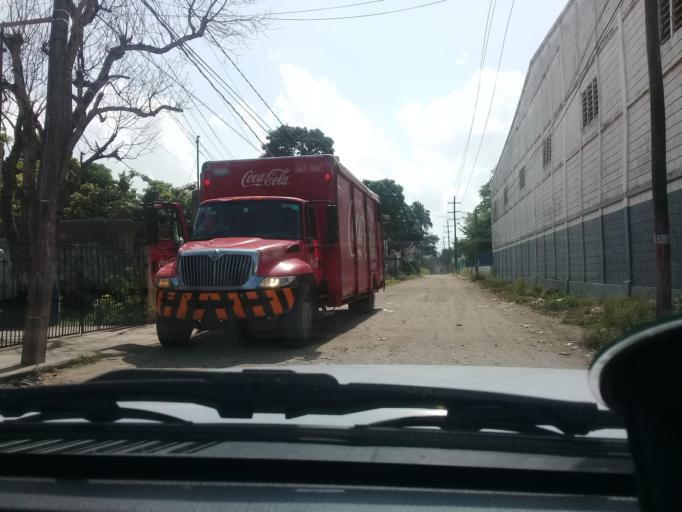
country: MX
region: Veracruz
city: Moralillo
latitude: 22.2261
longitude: -97.9019
